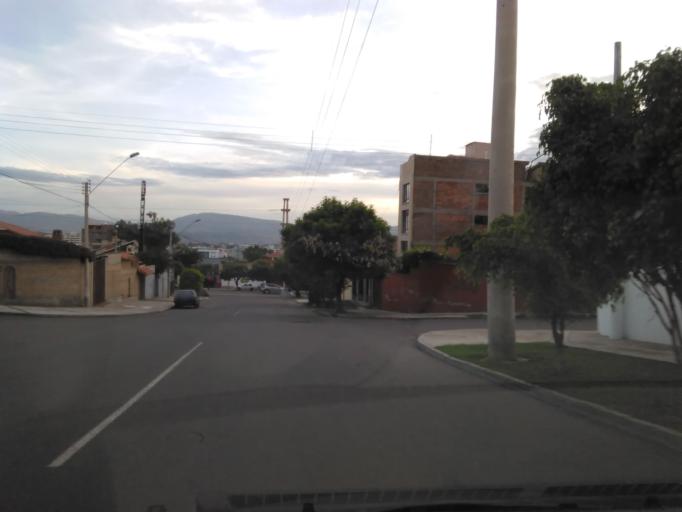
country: BO
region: Cochabamba
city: Cochabamba
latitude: -17.3645
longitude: -66.1606
